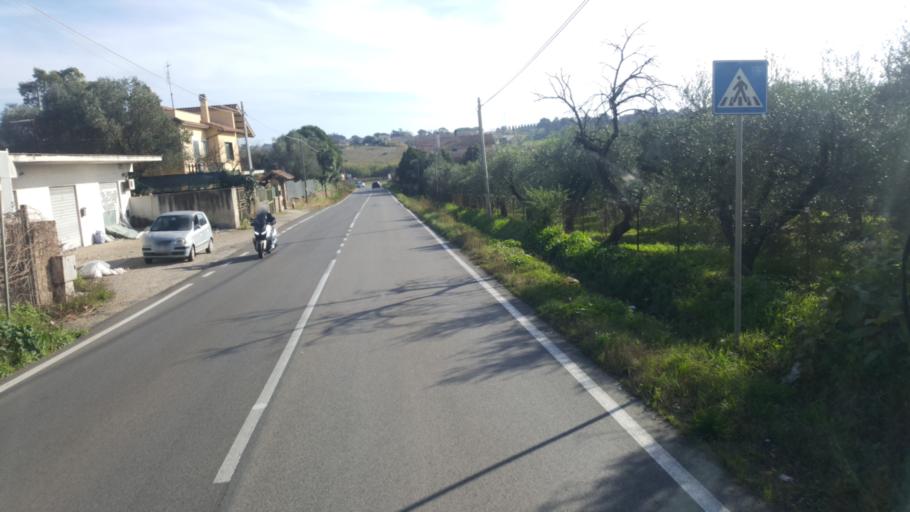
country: IT
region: Latium
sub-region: Citta metropolitana di Roma Capitale
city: Mantiglia di Ardea
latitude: 41.6760
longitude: 12.6291
